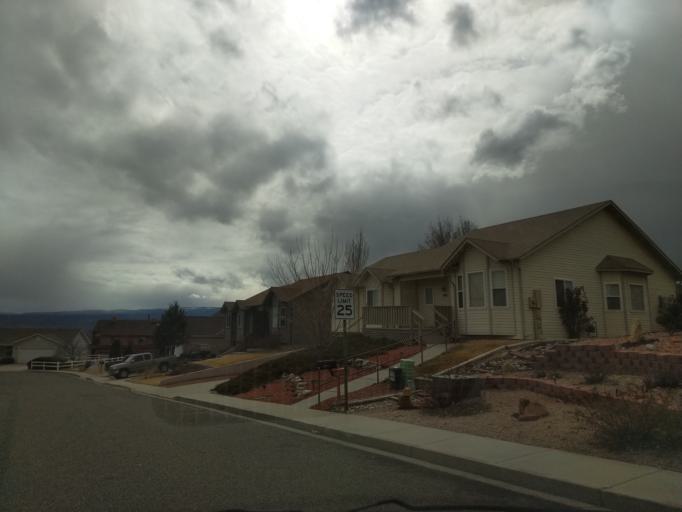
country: US
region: Colorado
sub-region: Mesa County
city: Fruitvale
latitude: 39.0913
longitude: -108.5265
